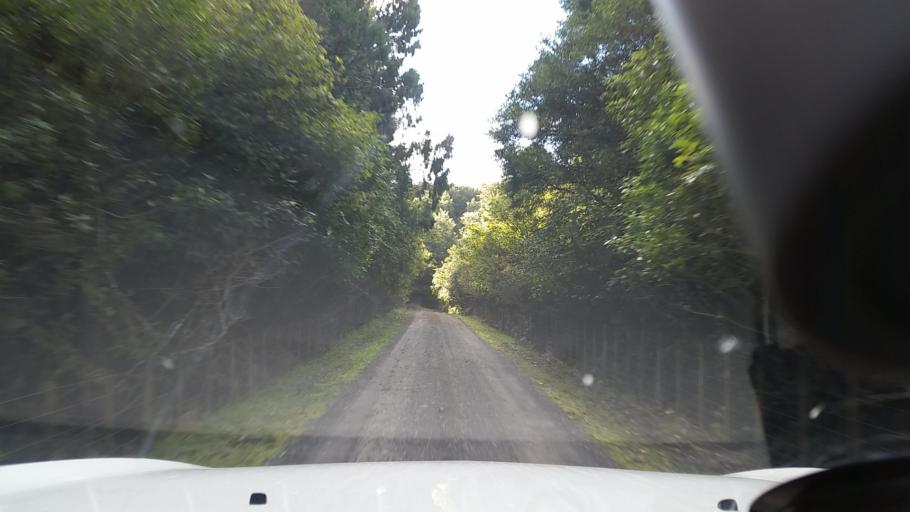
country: NZ
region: Bay of Plenty
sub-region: Rotorua District
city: Rotorua
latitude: -38.1092
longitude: 176.0520
